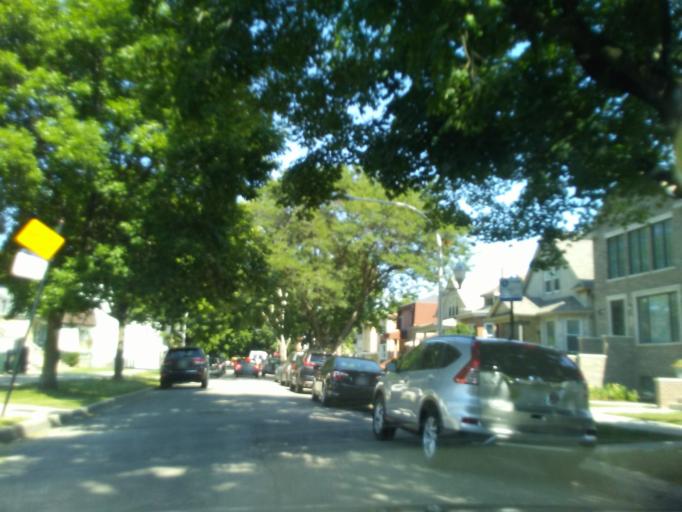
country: US
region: Illinois
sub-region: Cook County
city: Lincolnwood
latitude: 41.9716
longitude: -87.7563
